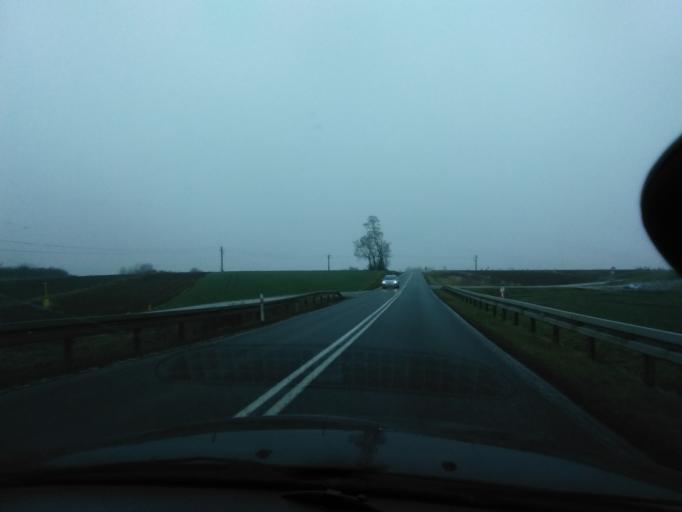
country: PL
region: Subcarpathian Voivodeship
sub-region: Powiat lancucki
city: Sonina
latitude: 50.0526
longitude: 22.2848
